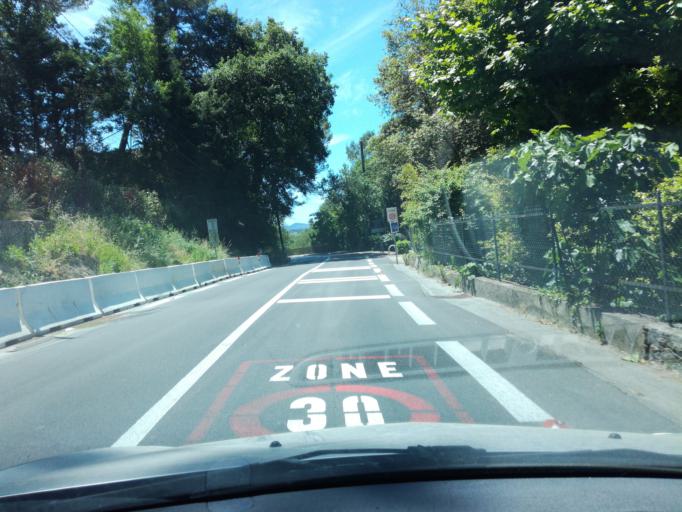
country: FR
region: Provence-Alpes-Cote d'Azur
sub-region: Departement des Alpes-Maritimes
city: Mougins
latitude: 43.5965
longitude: 7.0018
